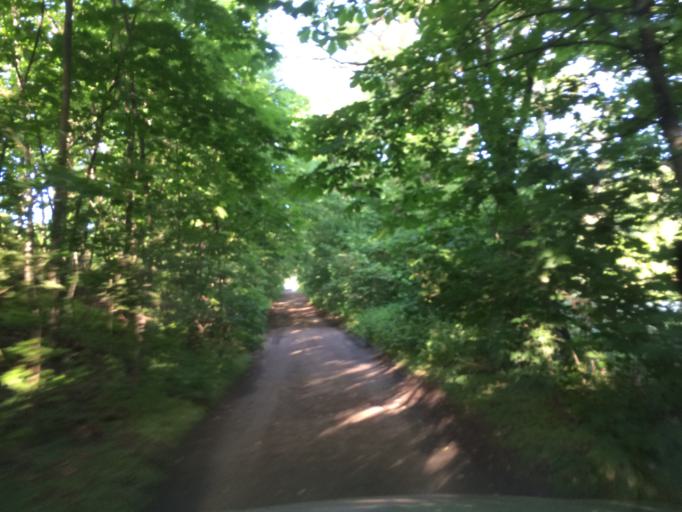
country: CZ
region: Praha
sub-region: Praha 4
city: Hodkovicky
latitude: 50.0369
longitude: 14.4491
